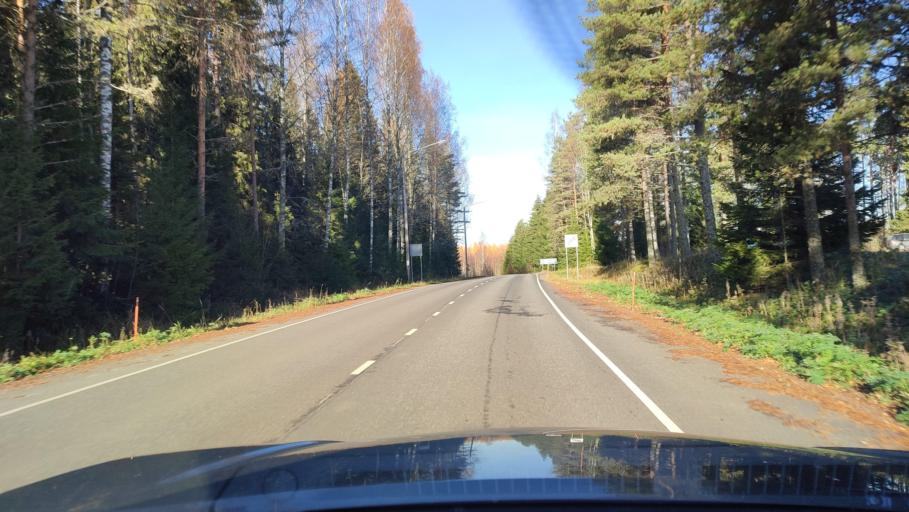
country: FI
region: Southern Ostrobothnia
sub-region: Suupohja
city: Karijoki
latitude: 62.3114
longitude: 21.7047
